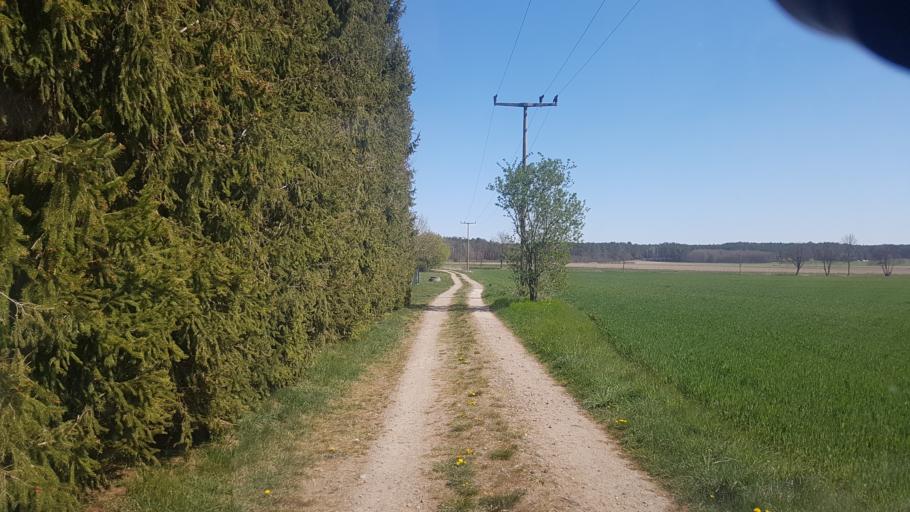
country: DE
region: Brandenburg
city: Sonnewalde
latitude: 51.7322
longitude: 13.6296
